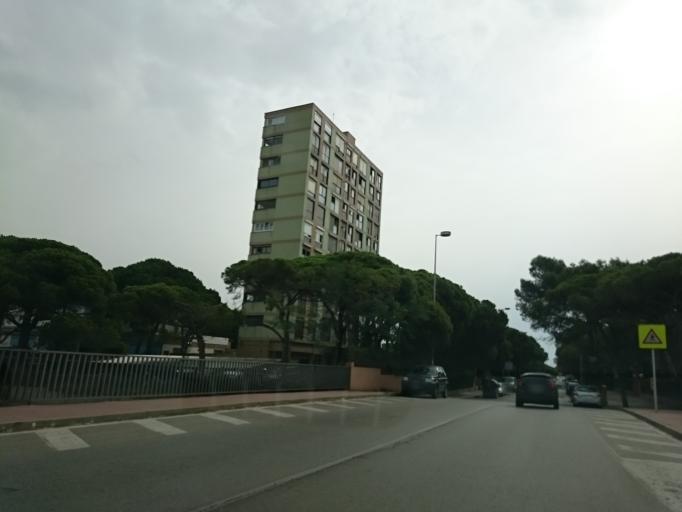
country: ES
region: Catalonia
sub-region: Provincia de Barcelona
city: Gava
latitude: 41.2686
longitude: 2.0105
